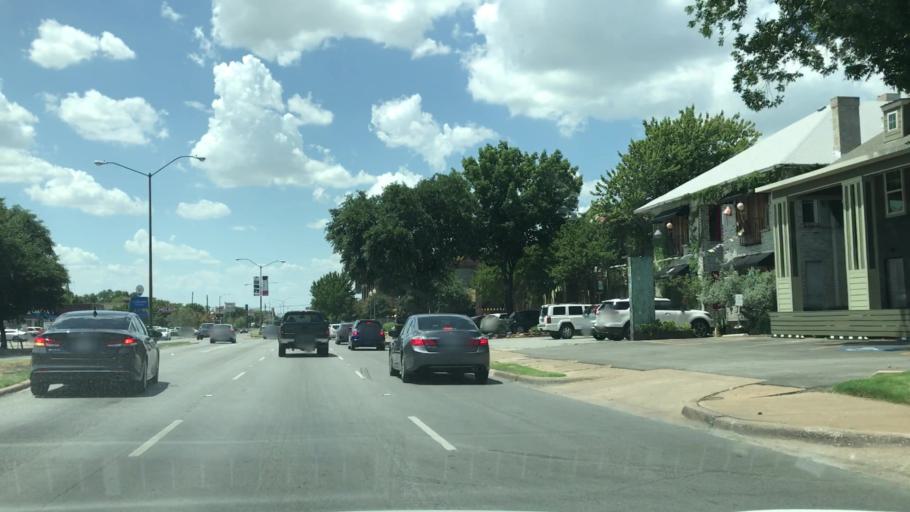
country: US
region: Texas
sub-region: Dallas County
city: Highland Park
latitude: 32.8144
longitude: -96.8084
